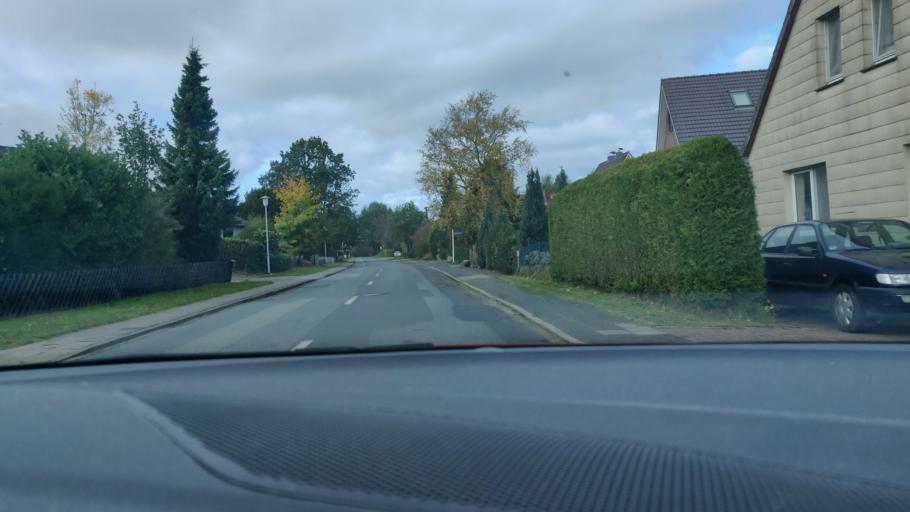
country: DE
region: Lower Saxony
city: Cuxhaven
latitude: 53.8305
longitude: 8.6692
